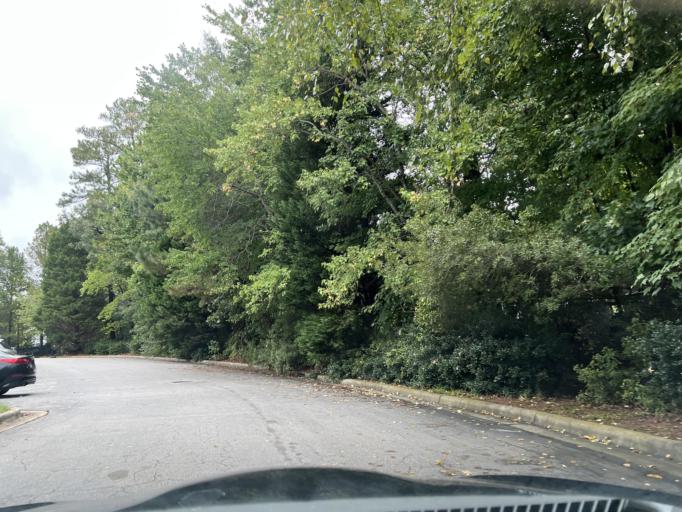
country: US
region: North Carolina
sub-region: Wake County
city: West Raleigh
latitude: 35.7498
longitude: -78.6936
